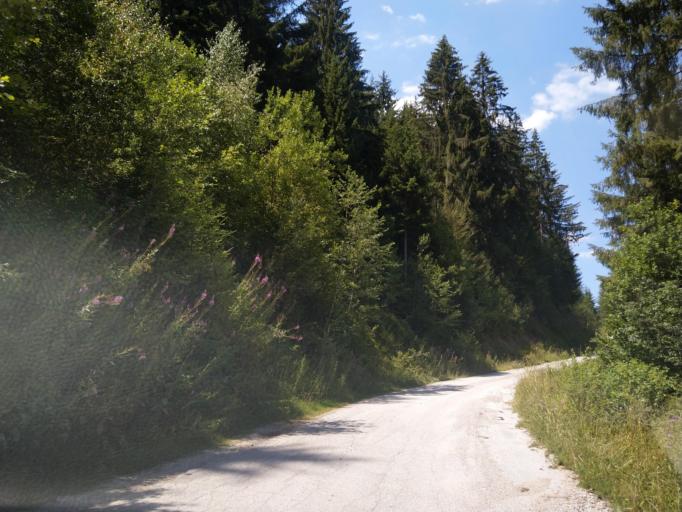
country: RS
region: Central Serbia
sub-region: Zlatiborski Okrug
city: Nova Varos
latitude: 43.4792
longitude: 19.9722
